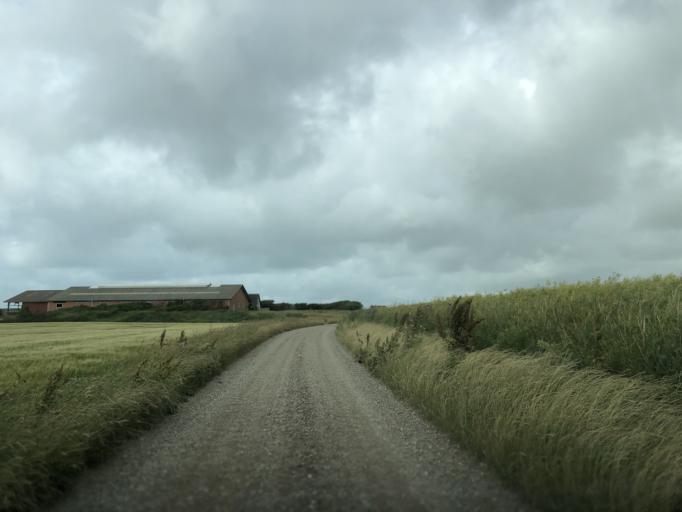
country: DK
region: Central Jutland
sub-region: Lemvig Kommune
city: Harboore
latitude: 56.5059
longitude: 8.1284
